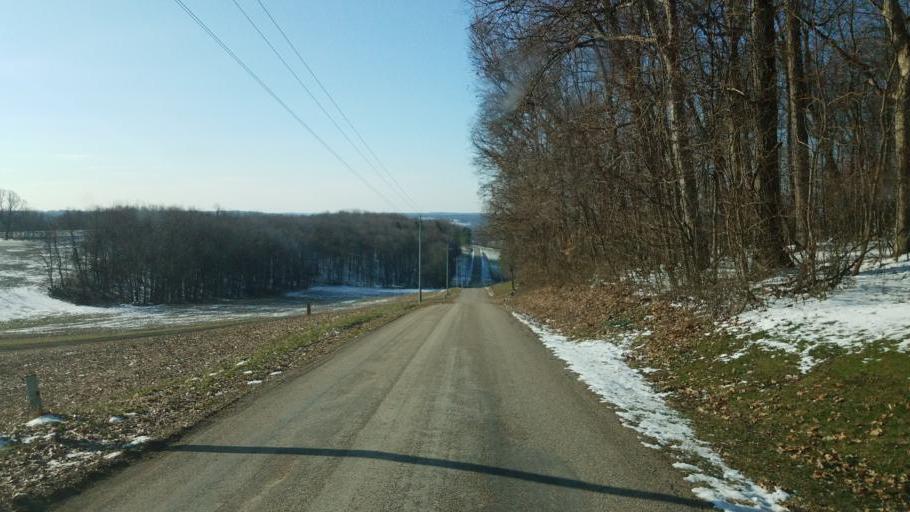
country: US
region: Ohio
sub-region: Sandusky County
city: Bellville
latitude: 40.5793
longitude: -82.4842
